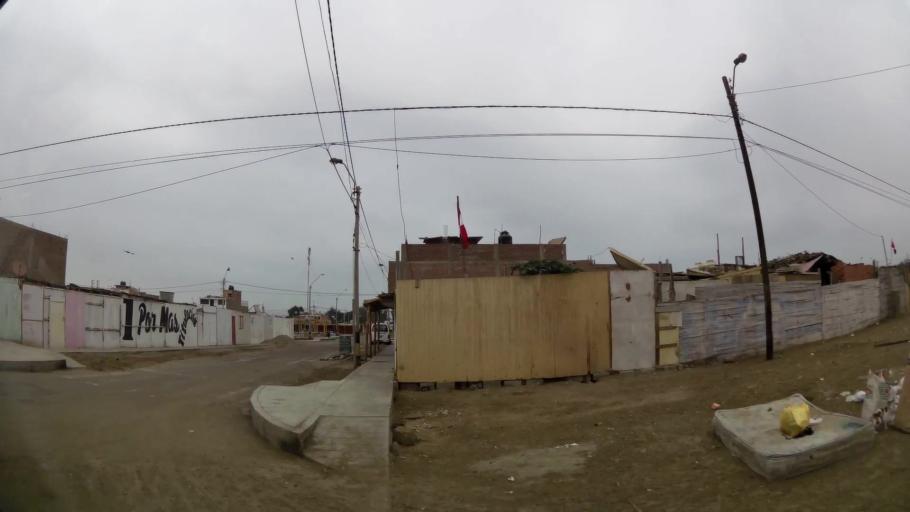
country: PE
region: Ica
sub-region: Provincia de Pisco
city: Paracas
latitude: -13.8361
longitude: -76.2471
